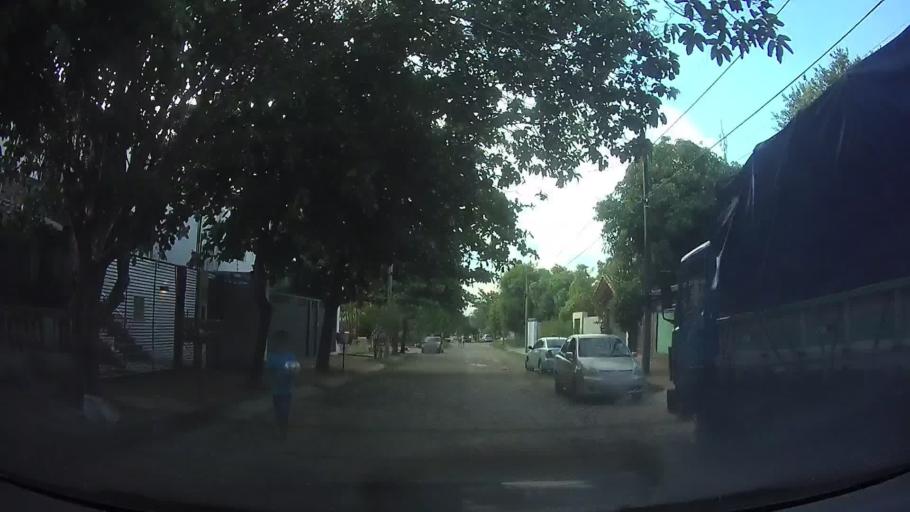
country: PY
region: Asuncion
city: Asuncion
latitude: -25.2668
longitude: -57.5742
